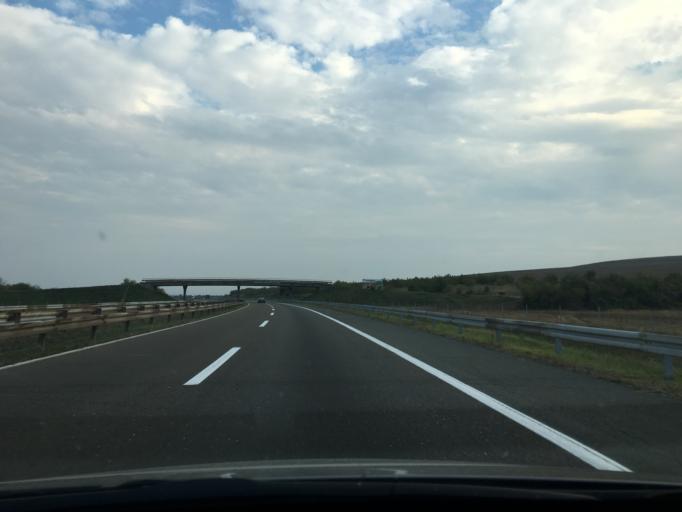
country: RS
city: Lugavcina
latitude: 44.4604
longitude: 21.0392
